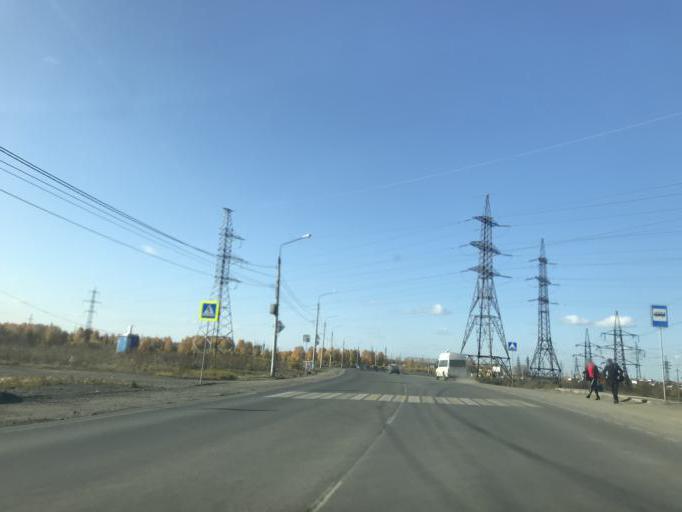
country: RU
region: Chelyabinsk
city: Roshchino
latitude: 55.2246
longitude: 61.2913
